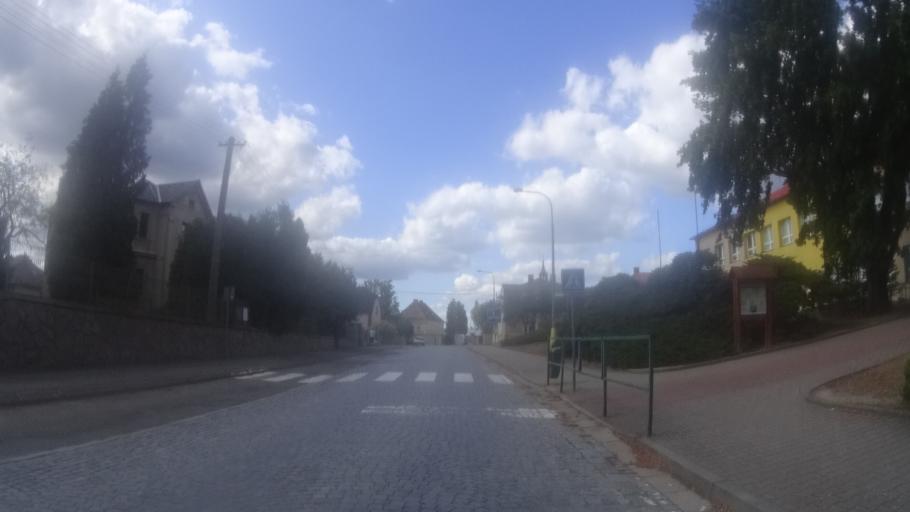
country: CZ
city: Borohradek
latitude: 50.0953
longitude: 16.0963
